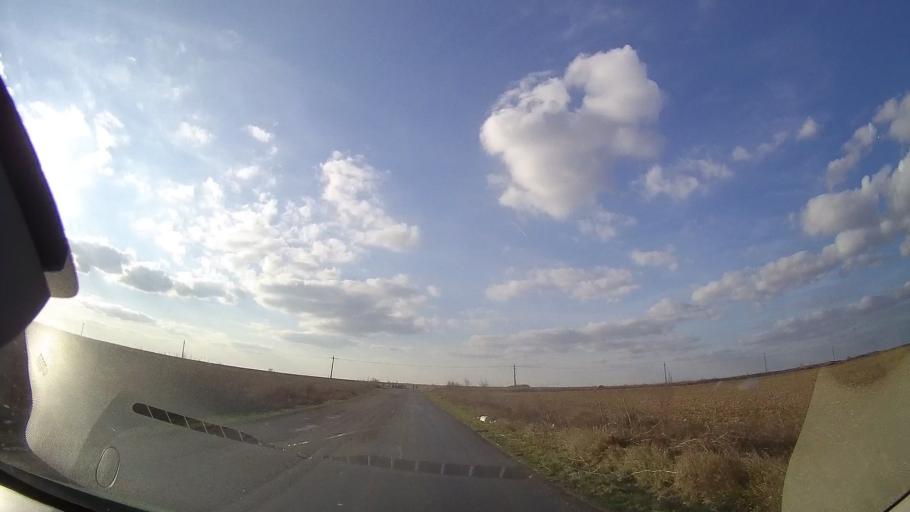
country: RO
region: Constanta
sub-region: Comuna Cerchezu
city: Cerchezu
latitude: 43.8261
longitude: 28.1262
